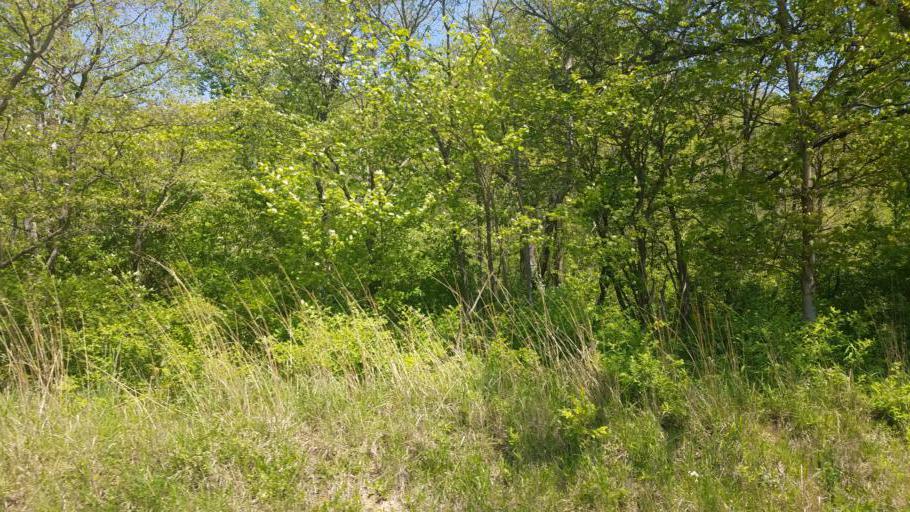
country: US
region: Ohio
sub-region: Licking County
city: Utica
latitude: 40.2482
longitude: -82.2859
